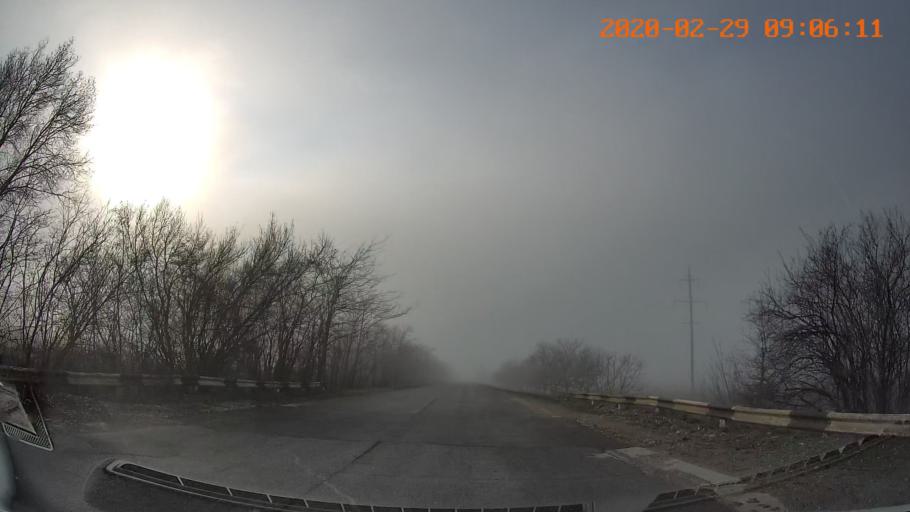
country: MD
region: Telenesti
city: Tiraspolul Nou
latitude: 46.8790
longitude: 29.7435
